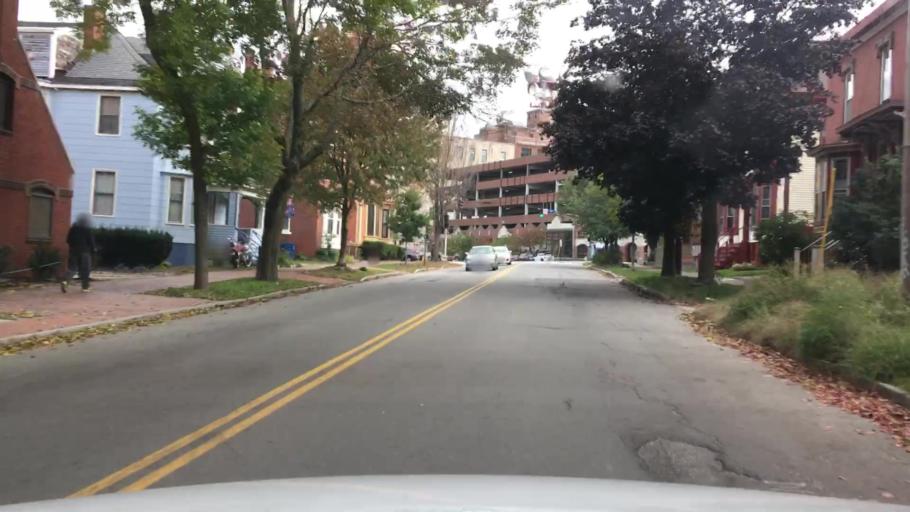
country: US
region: Maine
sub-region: Cumberland County
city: Portland
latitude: 43.6554
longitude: -70.2666
